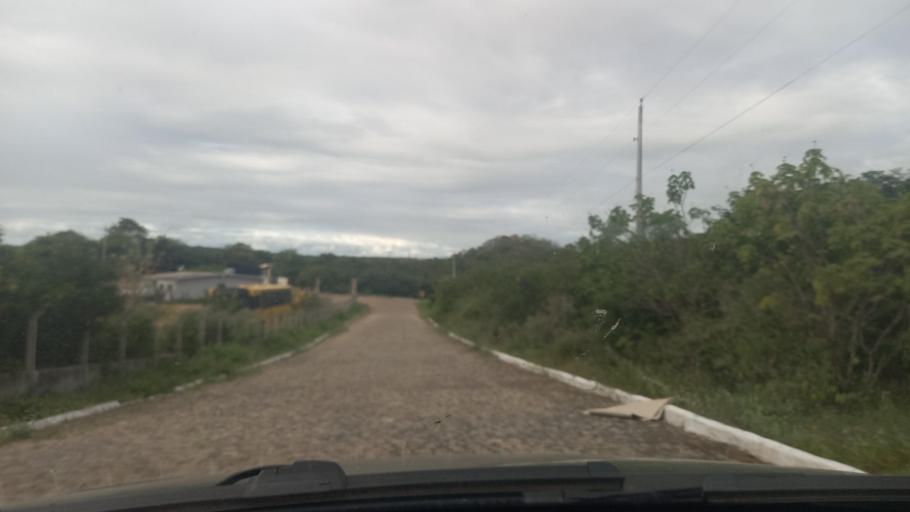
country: BR
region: Sergipe
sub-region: Caninde De Sao Francisco
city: Caninde de Sao Francisco
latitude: -9.6185
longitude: -37.8094
